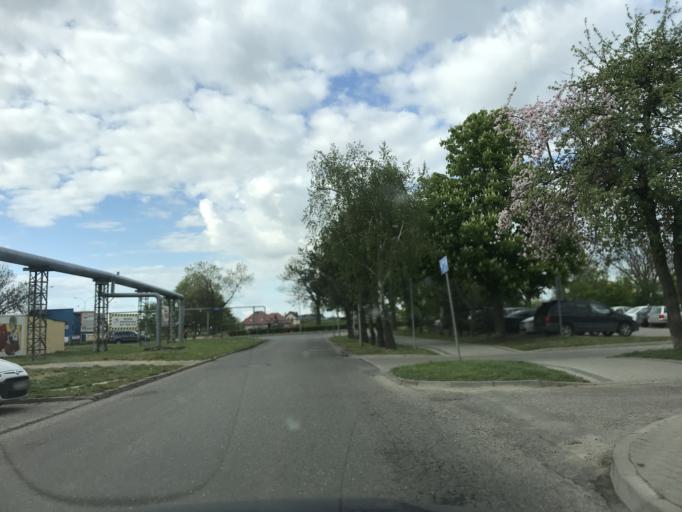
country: PL
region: West Pomeranian Voivodeship
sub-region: Powiat mysliborski
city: Mysliborz
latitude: 52.9267
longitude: 14.8776
